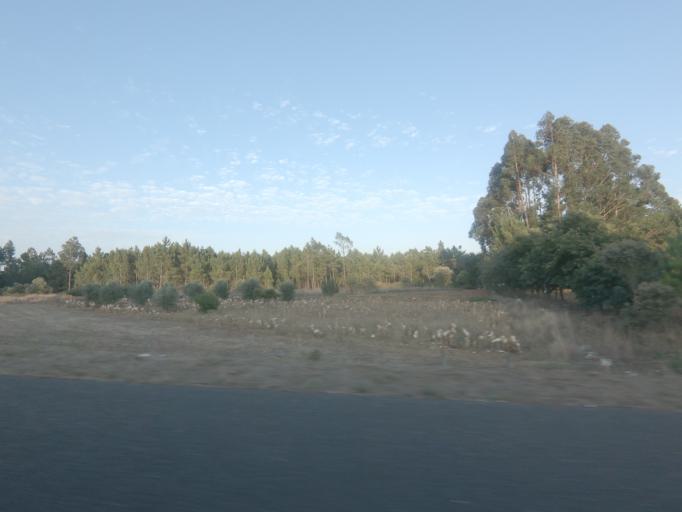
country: PT
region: Leiria
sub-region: Leiria
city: Santa Catarina da Serra
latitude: 39.6484
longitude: -8.6961
